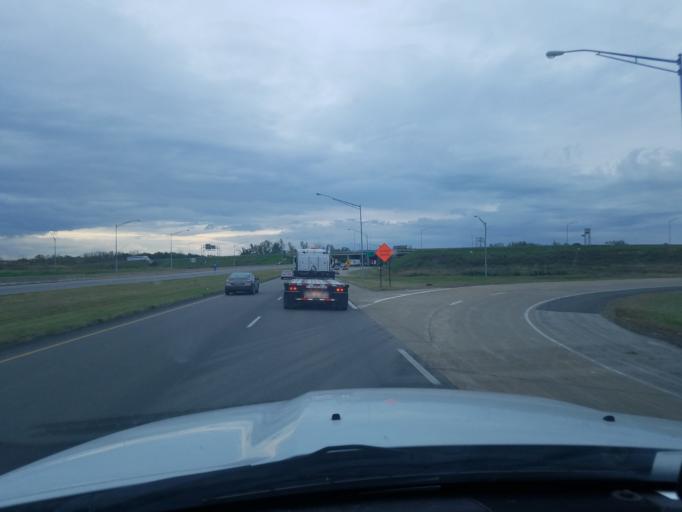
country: US
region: Indiana
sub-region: Vanderburgh County
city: Evansville
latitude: 37.9432
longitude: -87.5433
